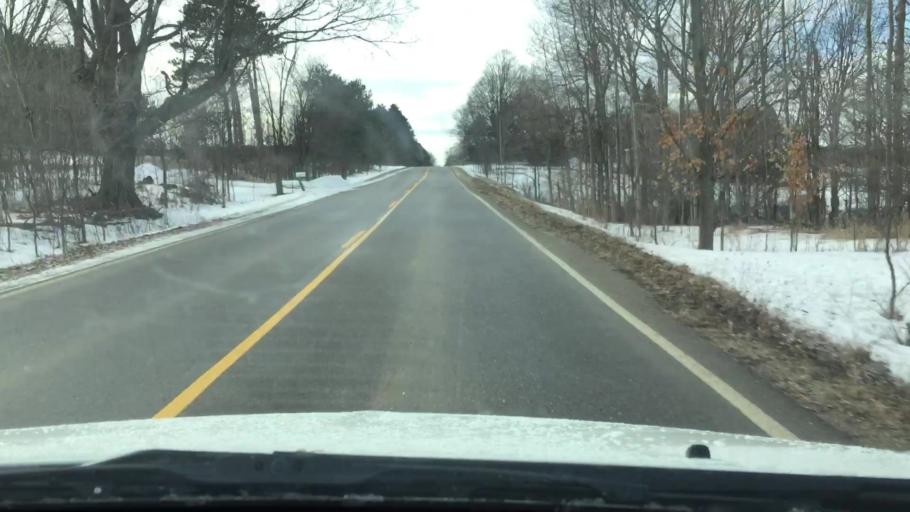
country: US
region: Michigan
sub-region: Wexford County
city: Manton
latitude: 44.4036
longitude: -85.4276
